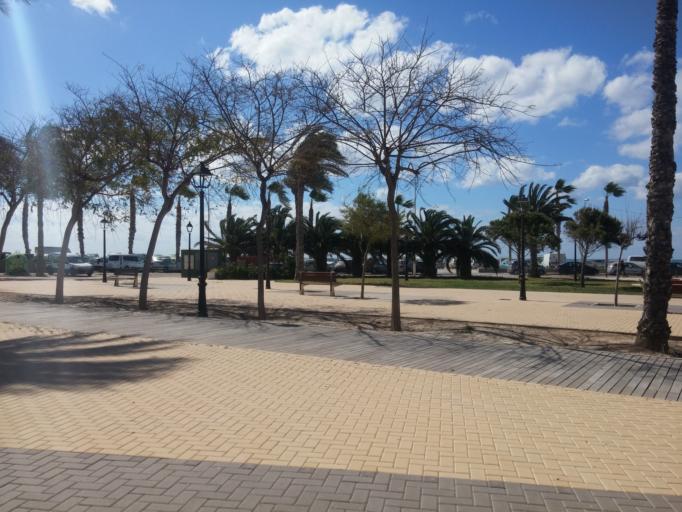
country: ES
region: Valencia
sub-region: Provincia de Alicante
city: Villajoyosa
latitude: 38.5028
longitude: -0.2331
